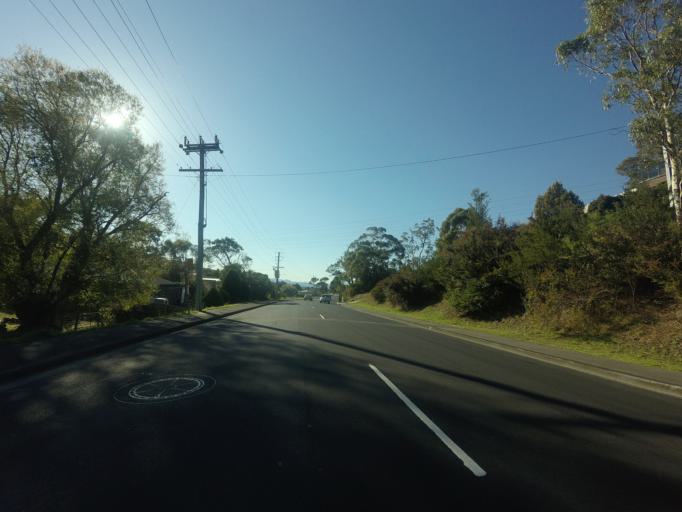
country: AU
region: Tasmania
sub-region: Glenorchy
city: West Moonah
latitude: -42.8522
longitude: 147.2681
